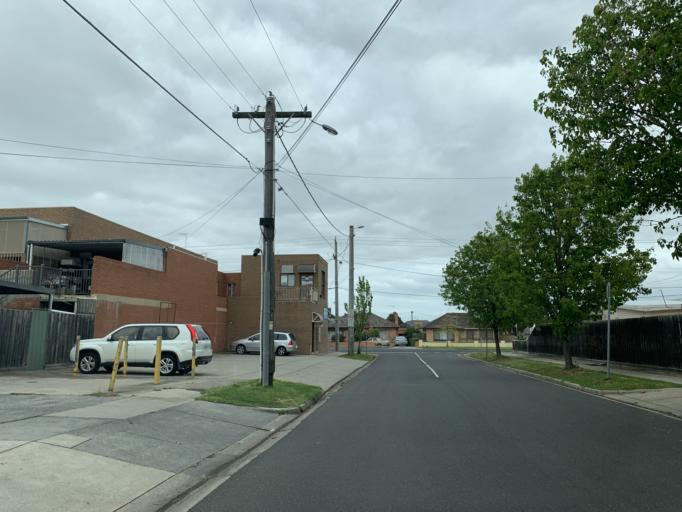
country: AU
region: Victoria
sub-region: Brimbank
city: St Albans
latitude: -37.7449
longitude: 144.8100
